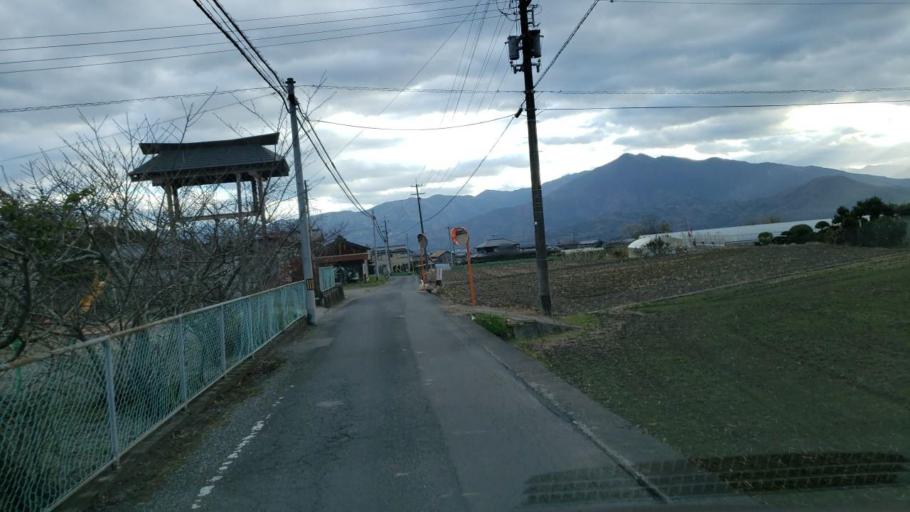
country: JP
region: Tokushima
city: Wakimachi
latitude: 34.1041
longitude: 134.2250
